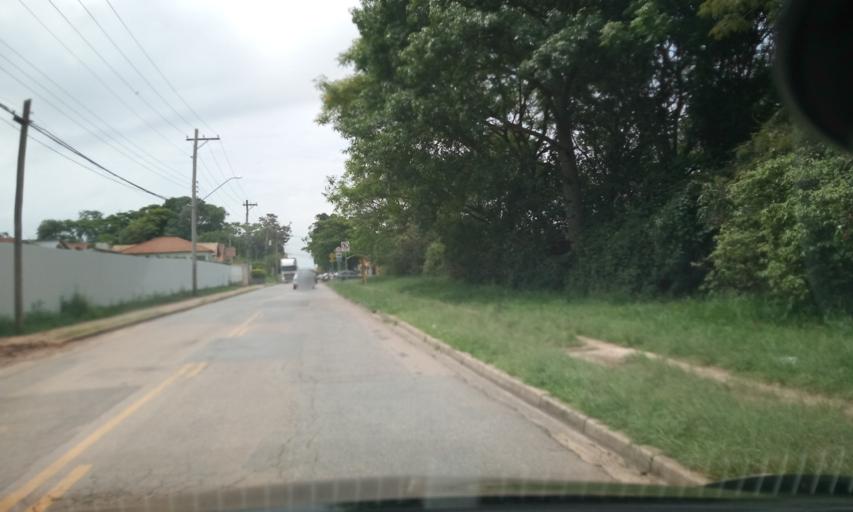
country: BR
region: Sao Paulo
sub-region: Itupeva
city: Itupeva
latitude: -23.1863
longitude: -46.9849
